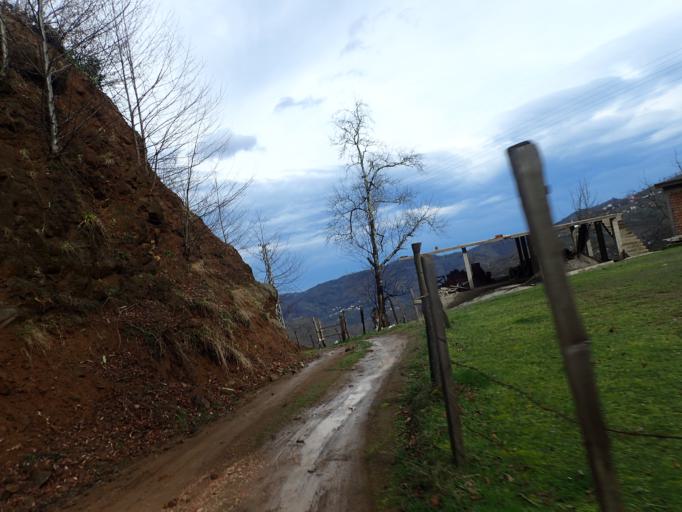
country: TR
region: Ordu
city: Camas
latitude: 40.8906
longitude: 37.5786
